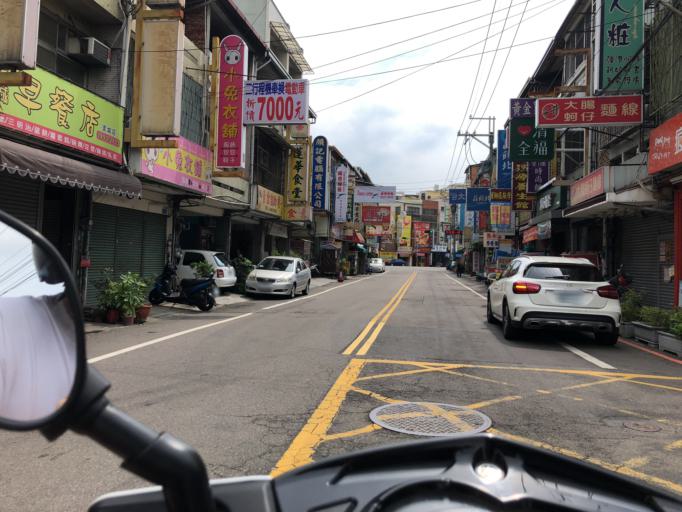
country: TW
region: Taiwan
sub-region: Taichung City
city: Taichung
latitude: 24.0909
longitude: 120.6941
